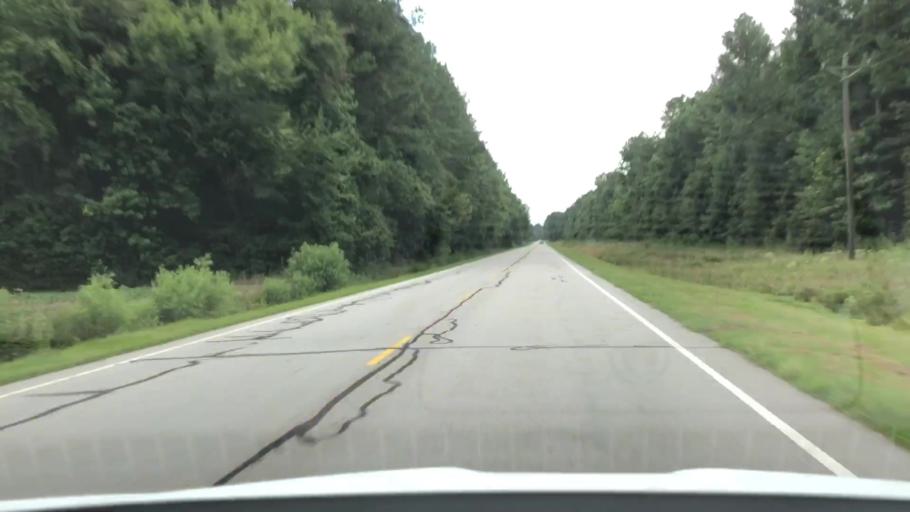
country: US
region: North Carolina
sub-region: Jones County
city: Trenton
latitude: 35.1120
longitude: -77.5079
